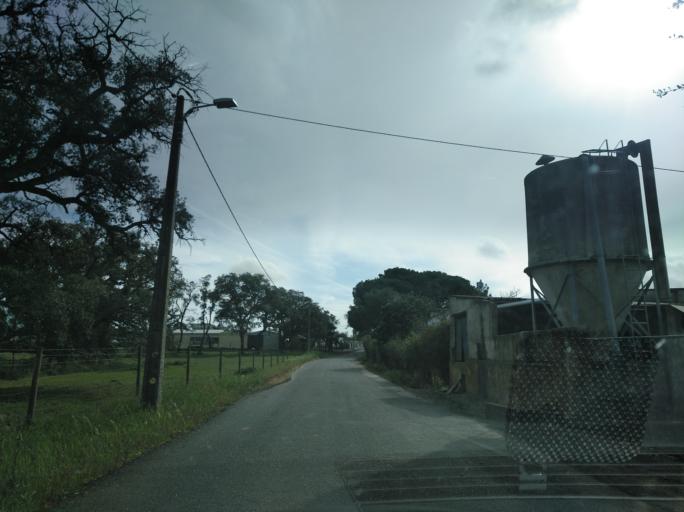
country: PT
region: Setubal
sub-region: Grandola
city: Grandola
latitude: 38.2009
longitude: -8.5455
